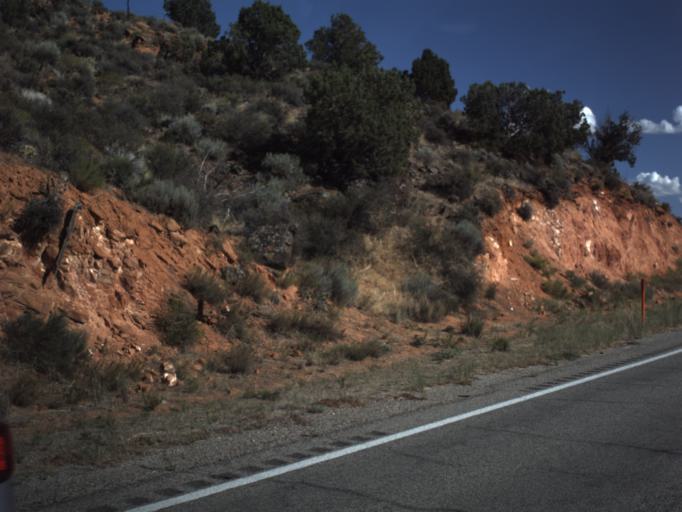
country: US
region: Utah
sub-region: Washington County
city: Toquerville
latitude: 37.2776
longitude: -113.3038
